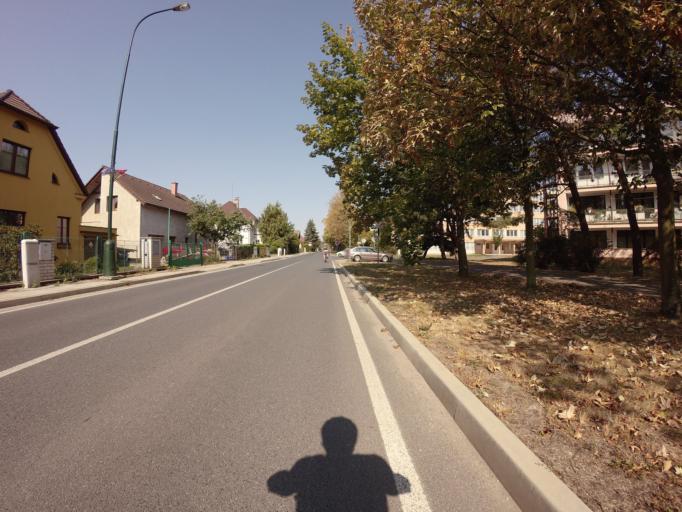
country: CZ
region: Central Bohemia
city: Tynec nad Sazavou
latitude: 49.8349
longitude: 14.5880
